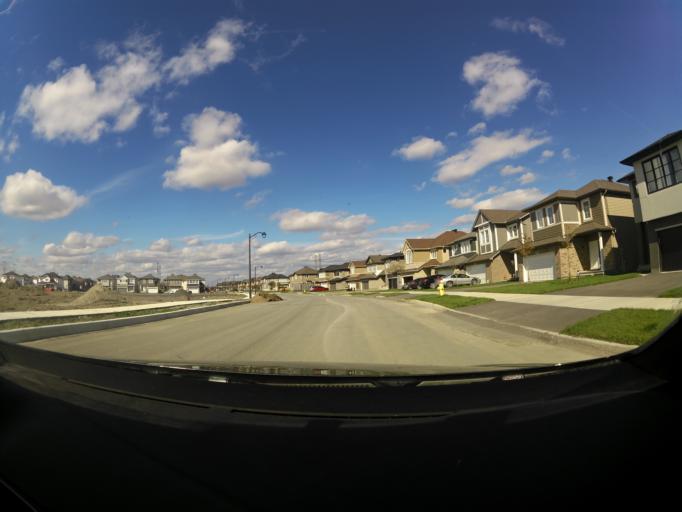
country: CA
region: Ontario
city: Bells Corners
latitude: 45.2759
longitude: -75.8807
